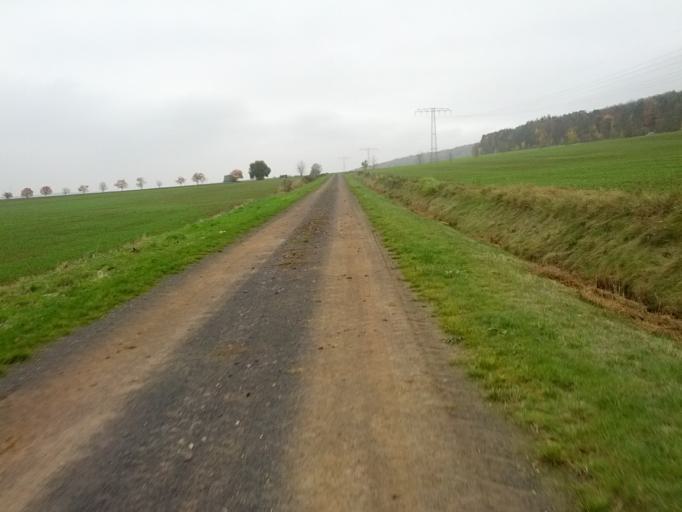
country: DE
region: Thuringia
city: Seebach
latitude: 50.9715
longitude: 10.4286
